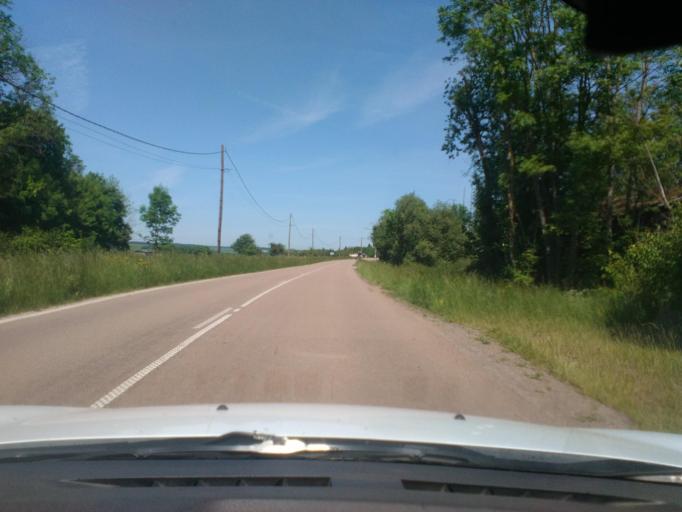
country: FR
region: Lorraine
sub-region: Departement des Vosges
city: Rambervillers
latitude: 48.3626
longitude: 6.6224
